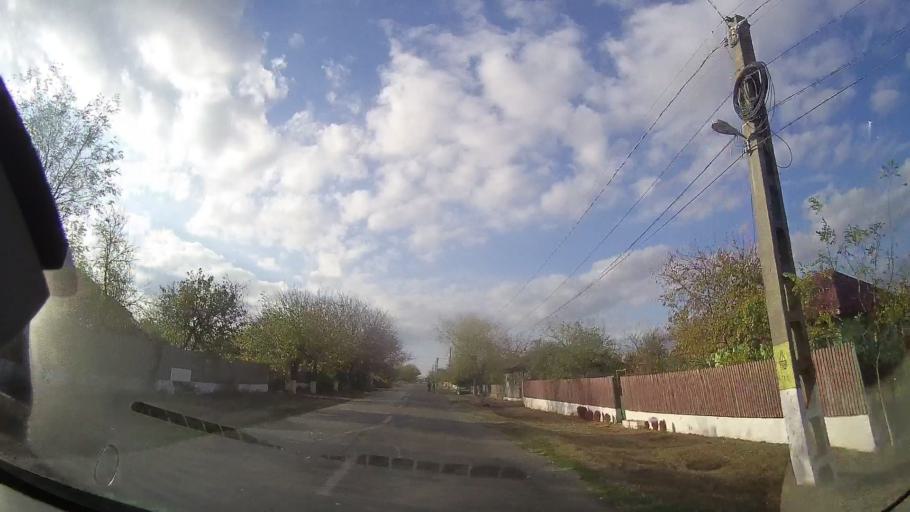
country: RO
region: Constanta
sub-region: Comuna Comana
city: Comana
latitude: 43.8228
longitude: 28.3380
